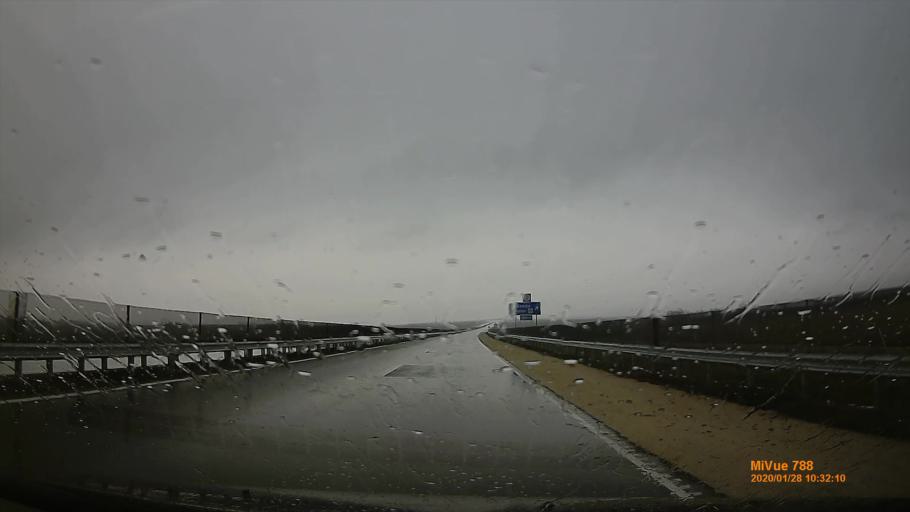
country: HU
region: Pest
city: Gomba
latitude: 47.3464
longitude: 19.4956
